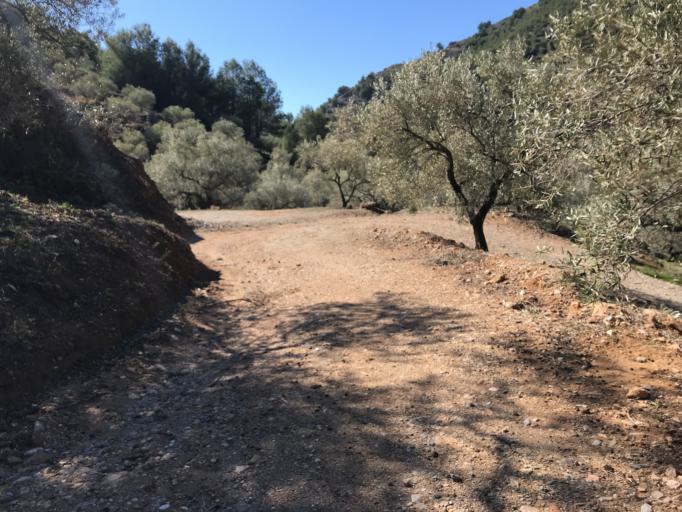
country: ES
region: Andalusia
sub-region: Provincia de Malaga
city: Canillas de Albaida
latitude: 36.8607
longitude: -3.9892
